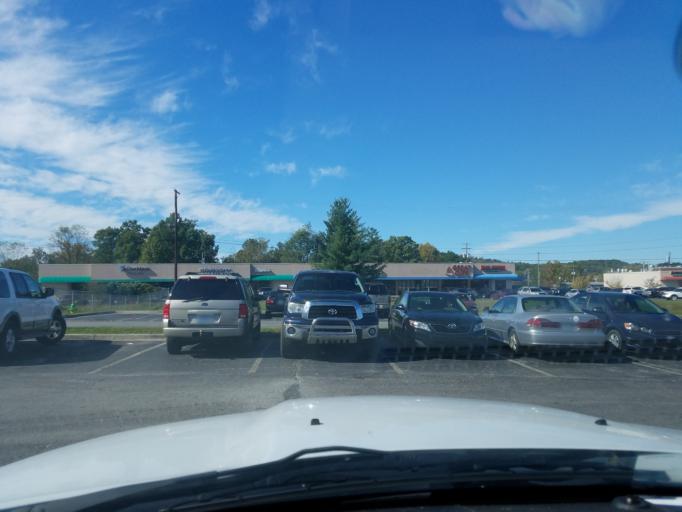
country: US
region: Kentucky
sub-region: Laurel County
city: London
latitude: 37.1074
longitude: -84.0901
